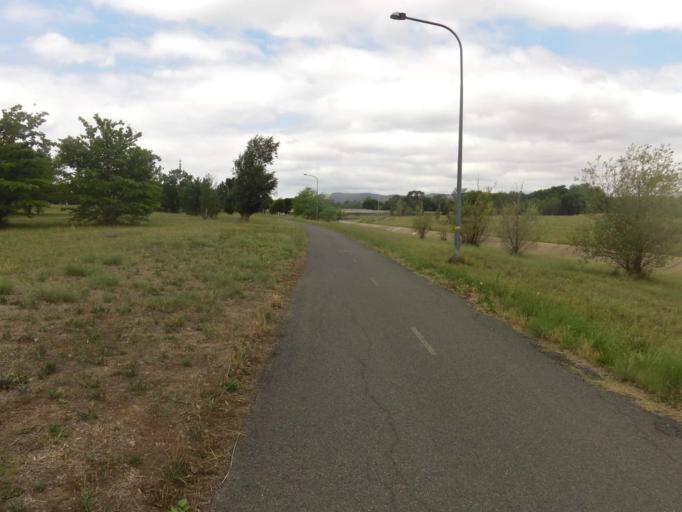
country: AU
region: Australian Capital Territory
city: Macarthur
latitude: -35.4218
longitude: 149.1004
